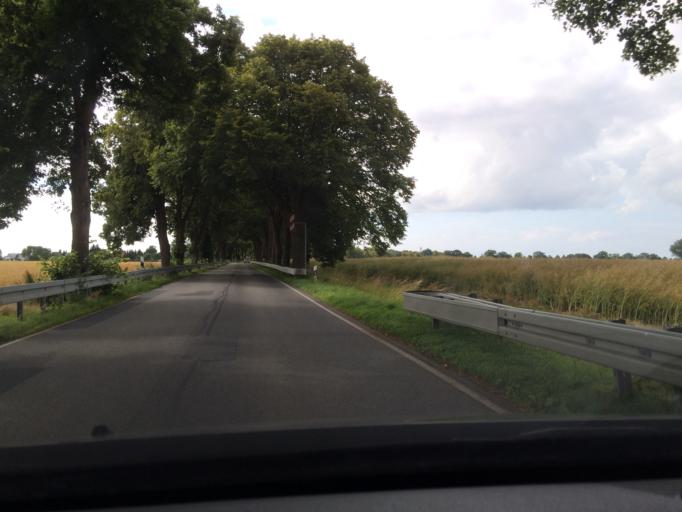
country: DE
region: Mecklenburg-Vorpommern
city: Prohn
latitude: 54.3811
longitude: 13.0100
